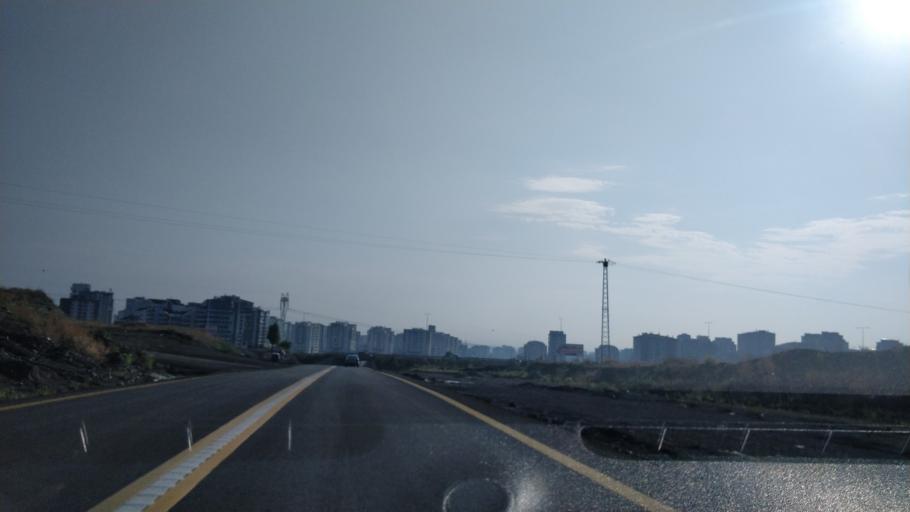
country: TR
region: Ankara
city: Etimesgut
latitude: 39.8841
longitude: 32.6097
